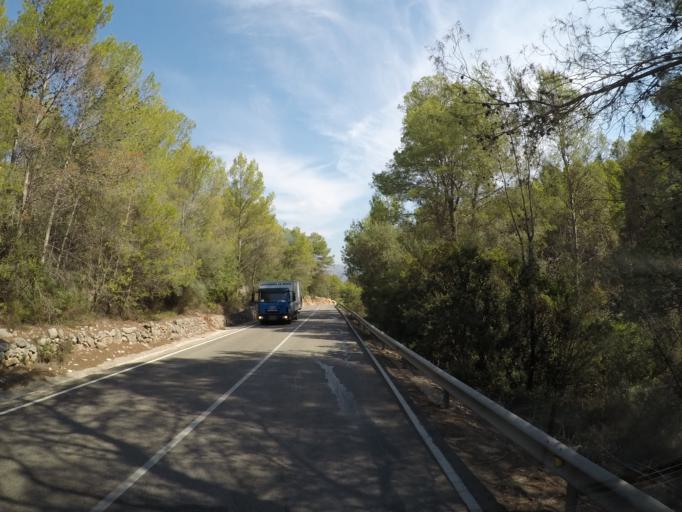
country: ES
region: Valencia
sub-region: Provincia de Alicante
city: Orba
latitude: 38.7795
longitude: -0.0792
